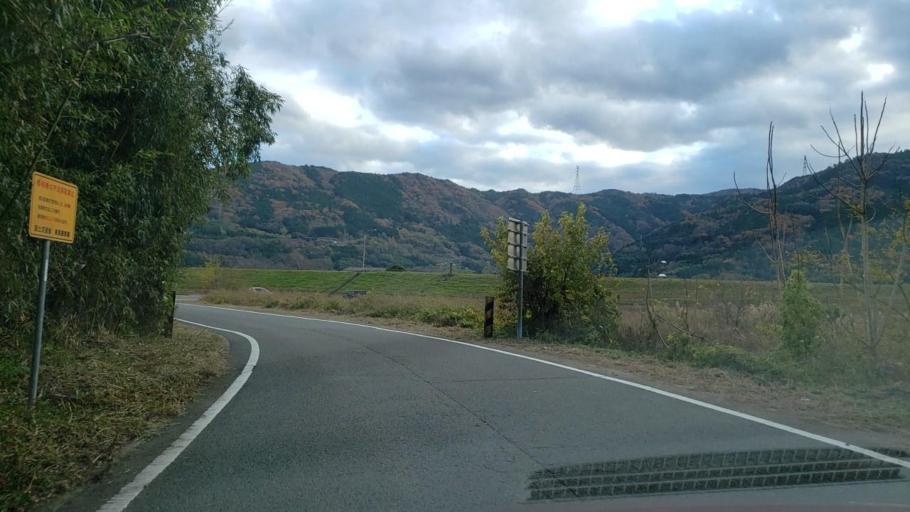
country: JP
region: Tokushima
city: Wakimachi
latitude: 34.0634
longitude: 134.1434
